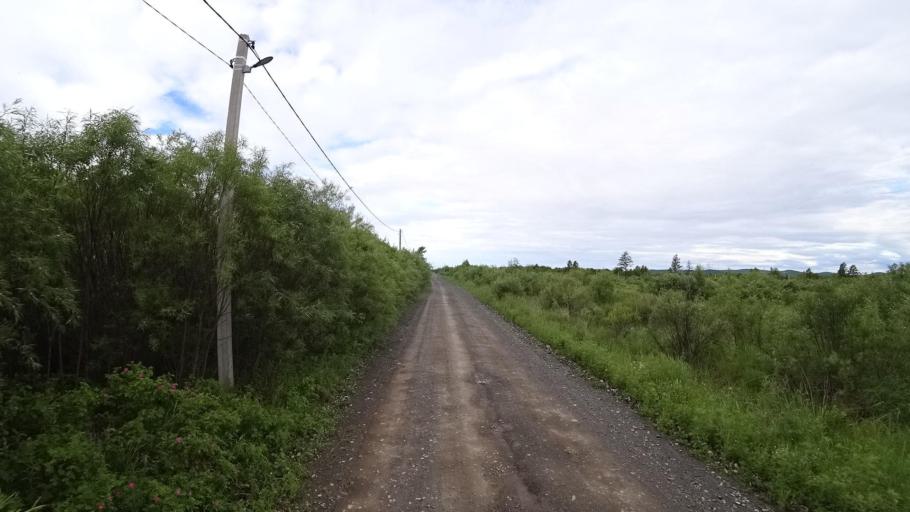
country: RU
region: Khabarovsk Krai
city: Amursk
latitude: 49.9085
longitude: 136.1493
